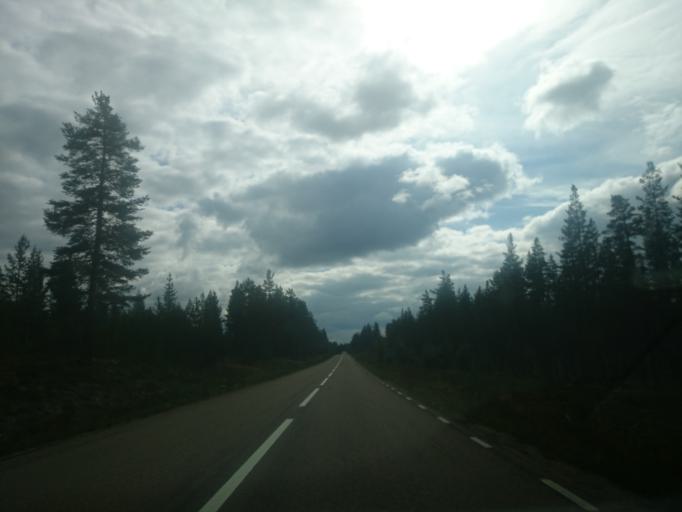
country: SE
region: Jaemtland
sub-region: Harjedalens Kommun
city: Sveg
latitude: 62.2545
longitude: 13.8405
